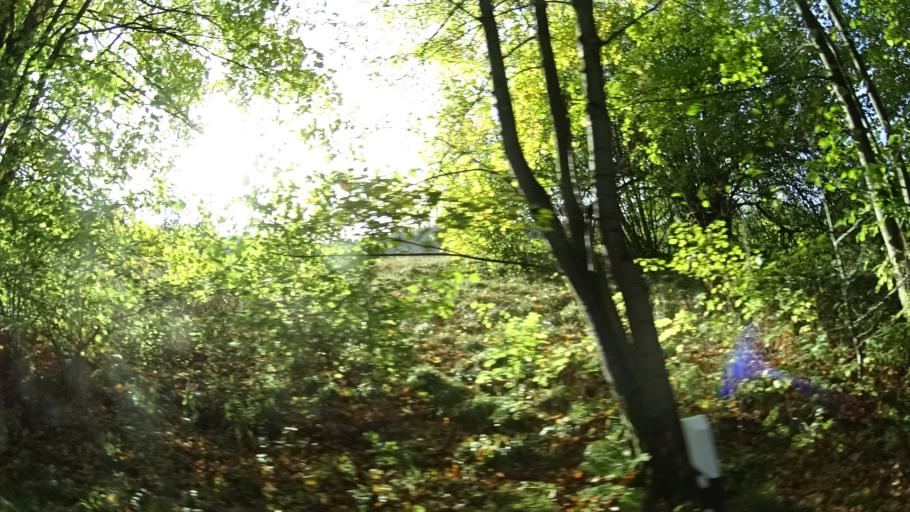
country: DE
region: Thuringia
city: Bermbach
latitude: 50.7026
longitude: 10.6259
